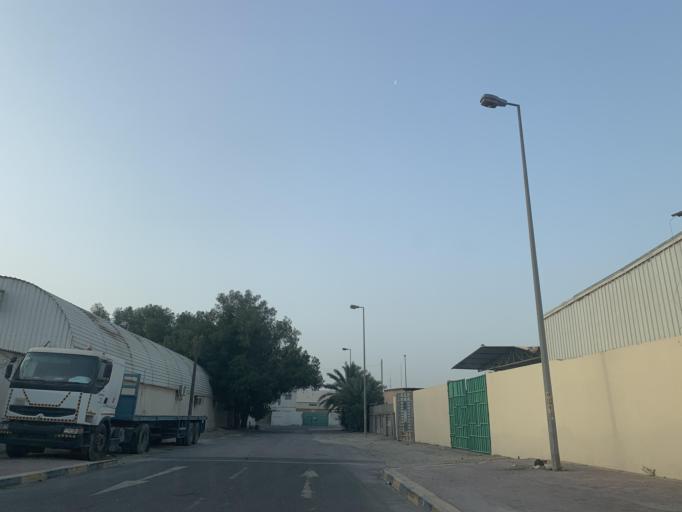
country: BH
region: Manama
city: Manama
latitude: 26.1981
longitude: 50.5943
